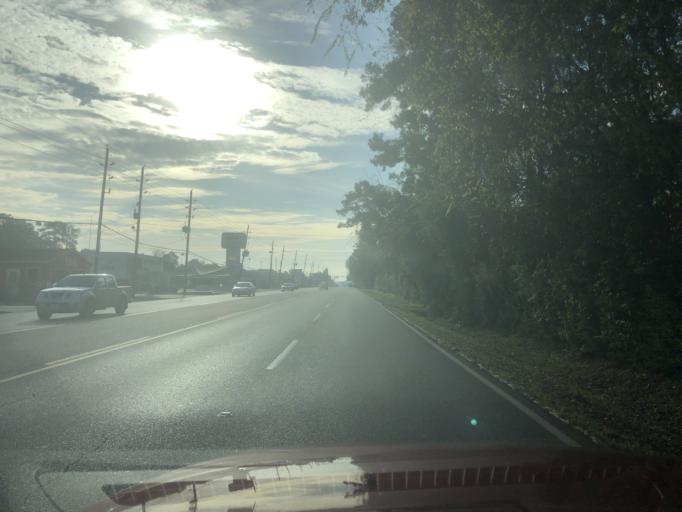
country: US
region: Texas
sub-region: Harris County
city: Spring
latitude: 30.0169
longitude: -95.4710
